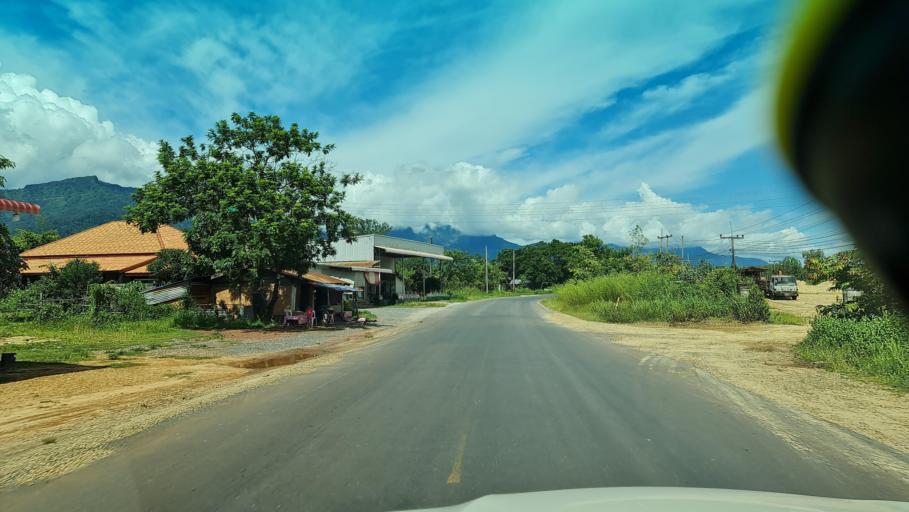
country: LA
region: Bolikhamxai
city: Ban Nahin
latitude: 18.3002
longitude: 104.1263
